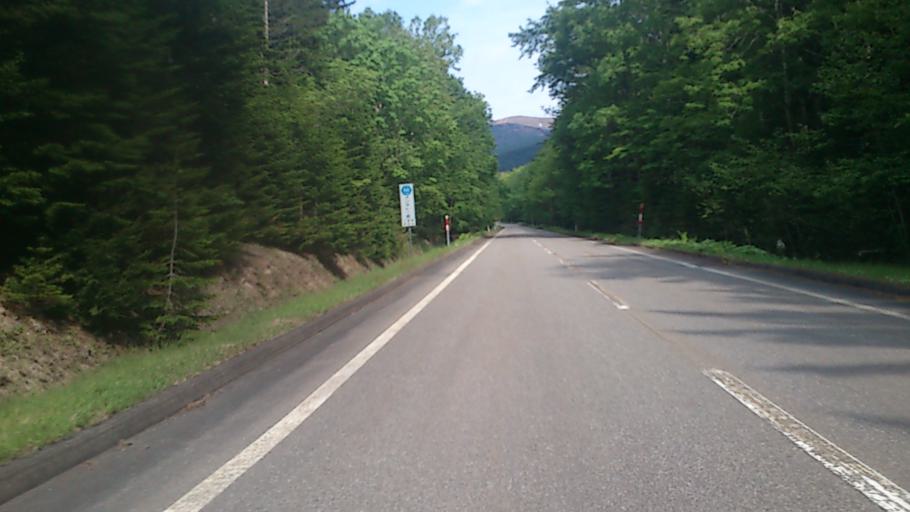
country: JP
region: Hokkaido
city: Kitami
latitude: 43.4020
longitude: 143.9732
